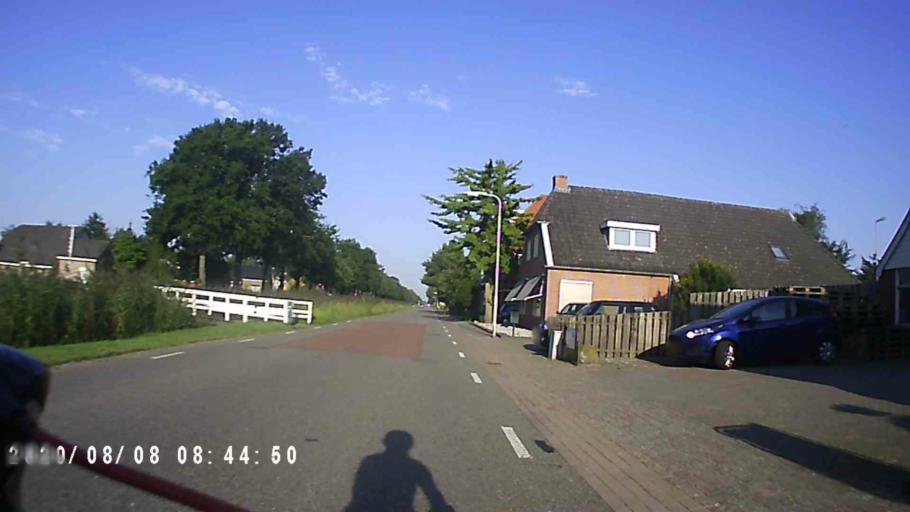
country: NL
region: Groningen
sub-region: Gemeente Leek
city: Leek
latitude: 53.0650
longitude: 6.3579
